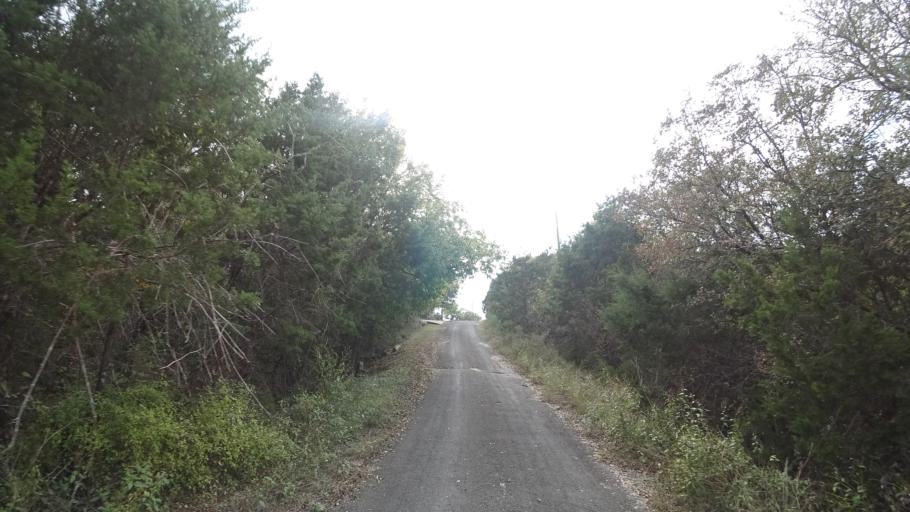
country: US
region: Texas
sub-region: Travis County
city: Hudson Bend
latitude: 30.3753
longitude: -97.9221
